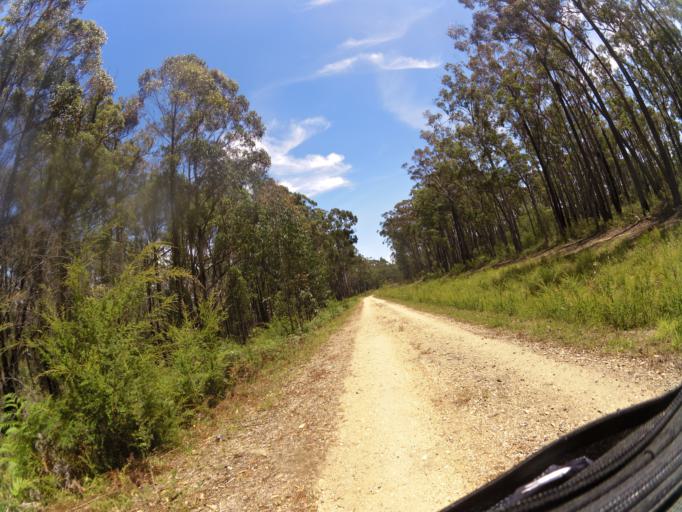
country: AU
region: Victoria
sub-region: East Gippsland
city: Lakes Entrance
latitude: -37.7592
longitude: 147.9404
